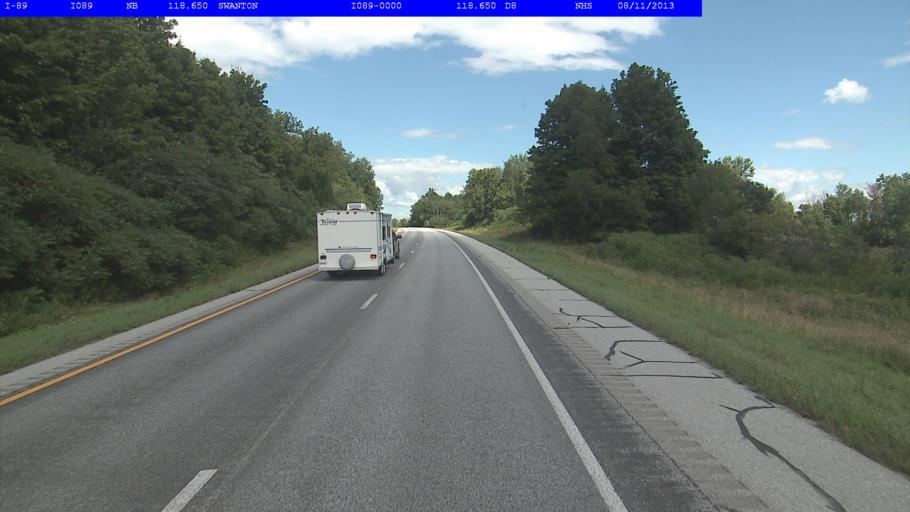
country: US
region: Vermont
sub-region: Franklin County
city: Saint Albans
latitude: 44.8578
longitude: -73.0805
